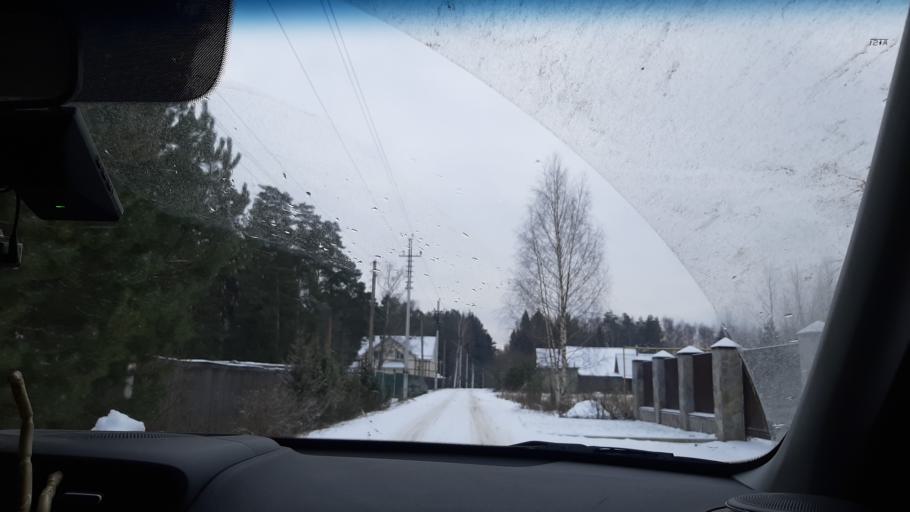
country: RU
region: Ivanovo
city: Kokhma
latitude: 56.9009
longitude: 41.0079
